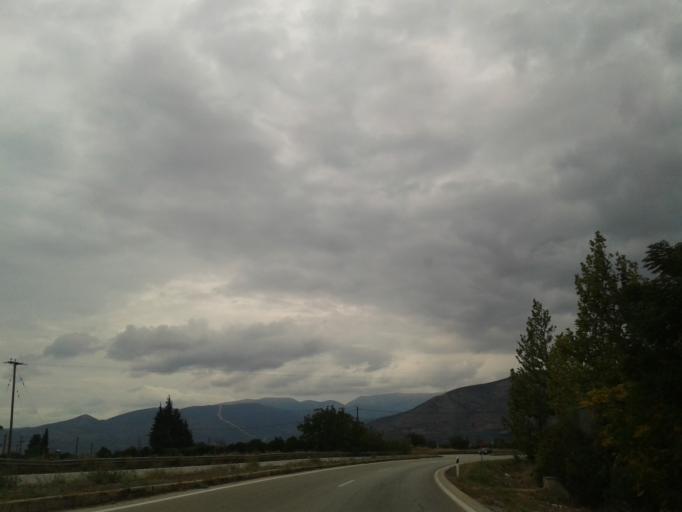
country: GR
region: Peloponnese
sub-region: Nomos Argolidos
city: Argos
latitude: 37.6153
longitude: 22.7278
